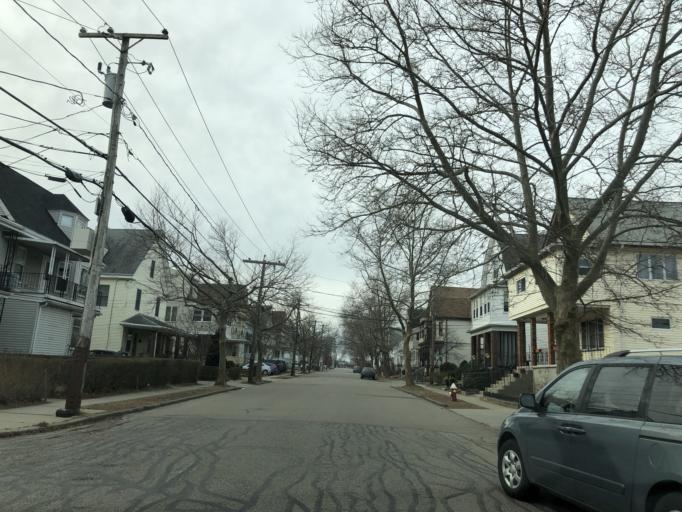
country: US
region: Massachusetts
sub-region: Middlesex County
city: Watertown
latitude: 42.3682
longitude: -71.1612
